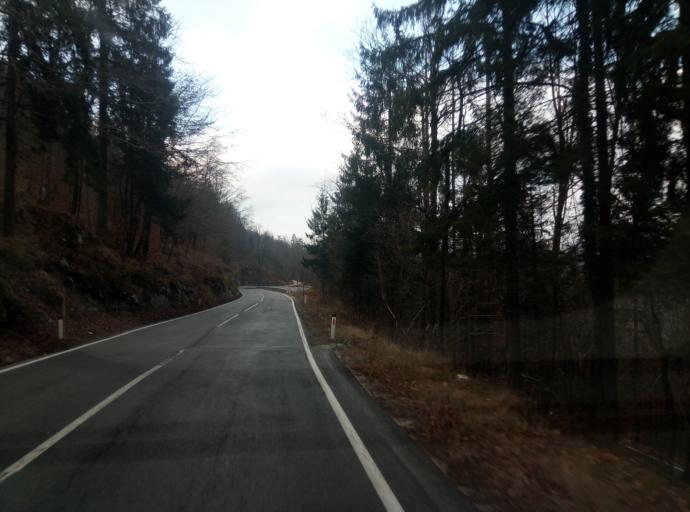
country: SI
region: Idrija
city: Idrija
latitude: 45.9535
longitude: 14.0777
